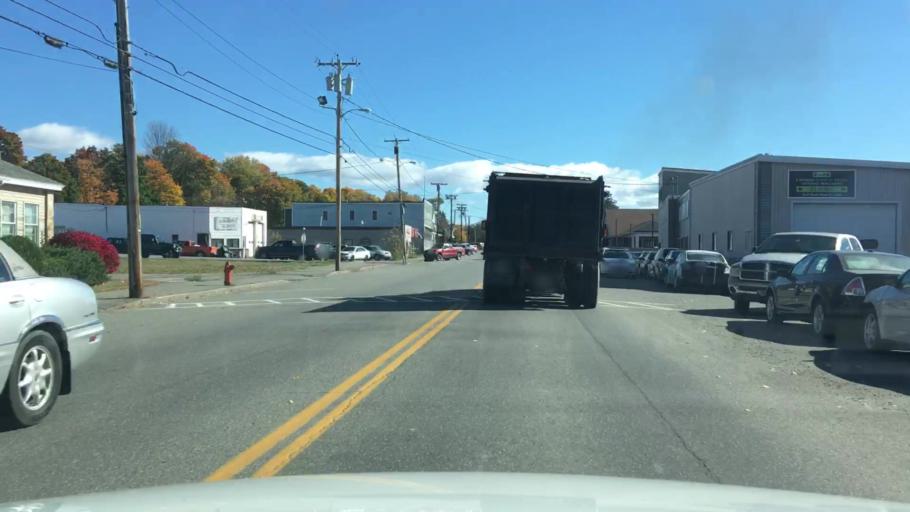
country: US
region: Maine
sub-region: Penobscot County
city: East Millinocket
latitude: 45.6261
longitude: -68.5780
